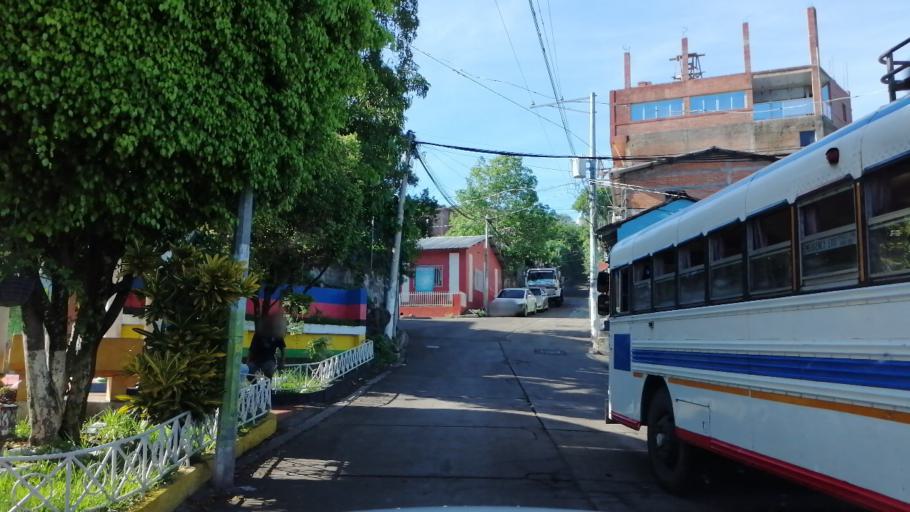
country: SV
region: Morazan
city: Cacaopera
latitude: 13.7734
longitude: -88.0795
